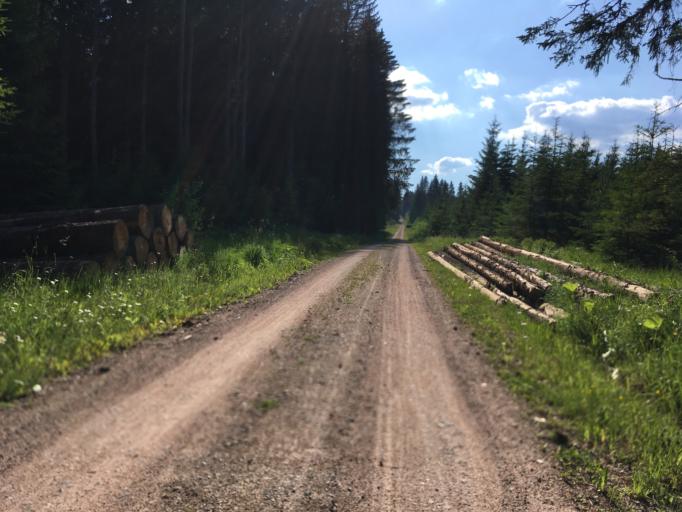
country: DE
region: Baden-Wuerttemberg
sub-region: Freiburg Region
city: Loffingen
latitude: 47.9349
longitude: 8.3209
